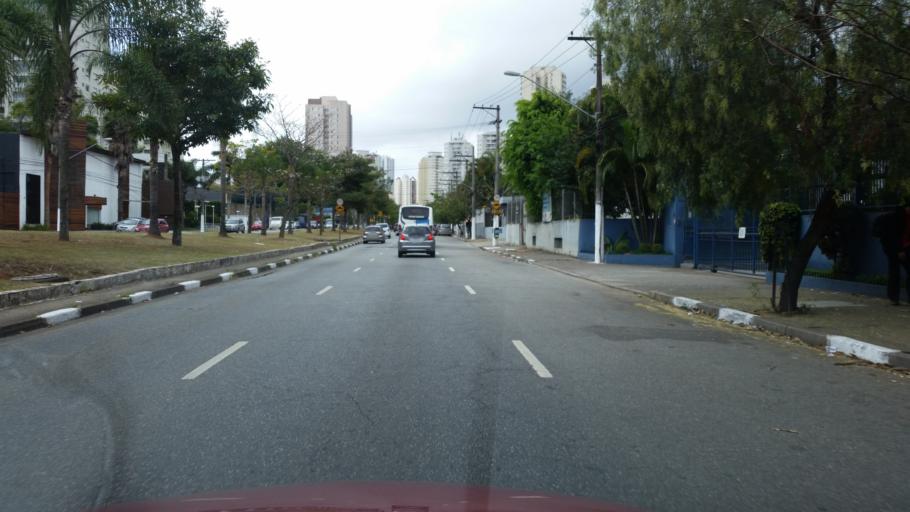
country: BR
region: Sao Paulo
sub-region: Diadema
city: Diadema
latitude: -23.6678
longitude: -46.6950
